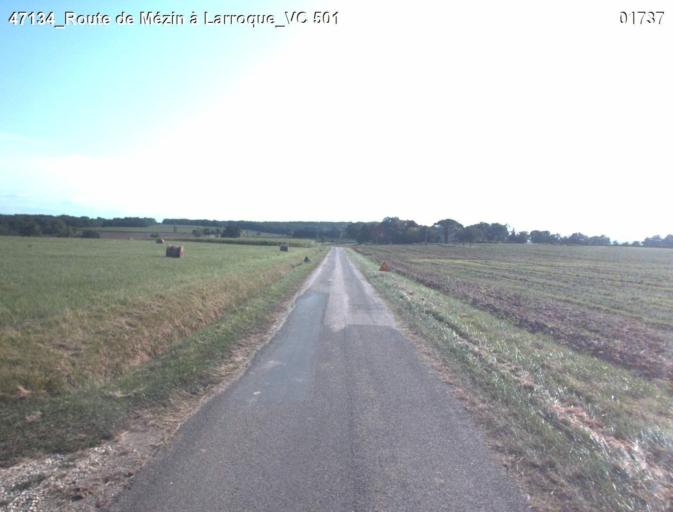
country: FR
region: Aquitaine
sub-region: Departement du Lot-et-Garonne
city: Mezin
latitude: 44.0132
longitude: 0.2774
